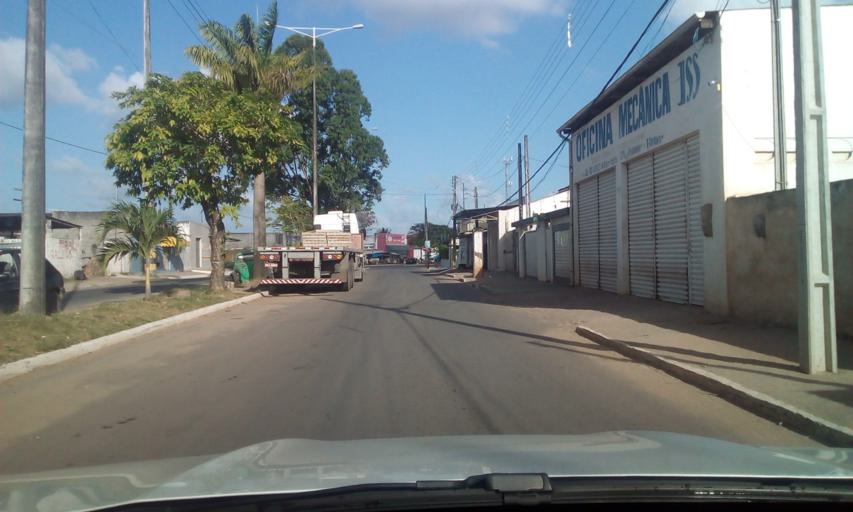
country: BR
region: Paraiba
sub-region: Conde
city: Conde
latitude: -7.1958
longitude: -34.8858
